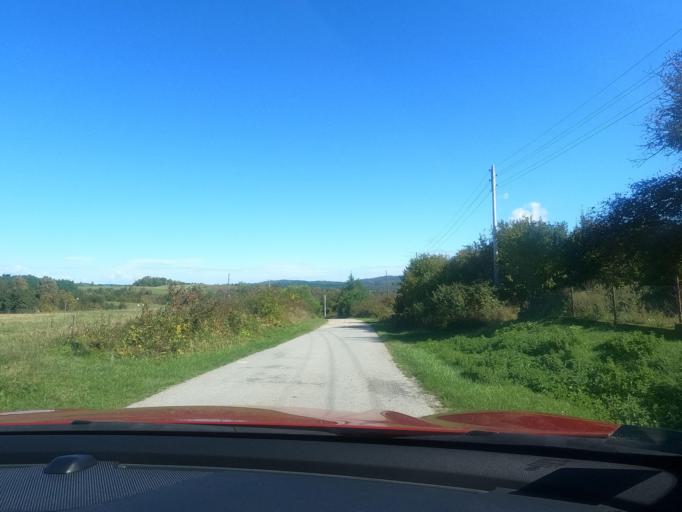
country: HR
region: Sisacko-Moslavacka
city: Petrinja
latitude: 45.3539
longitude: 16.2172
